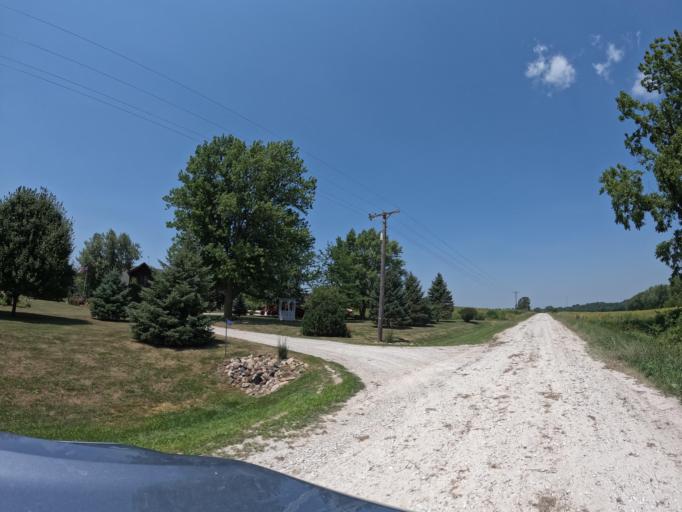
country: US
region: Iowa
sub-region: Keokuk County
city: Sigourney
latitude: 41.2956
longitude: -92.2095
